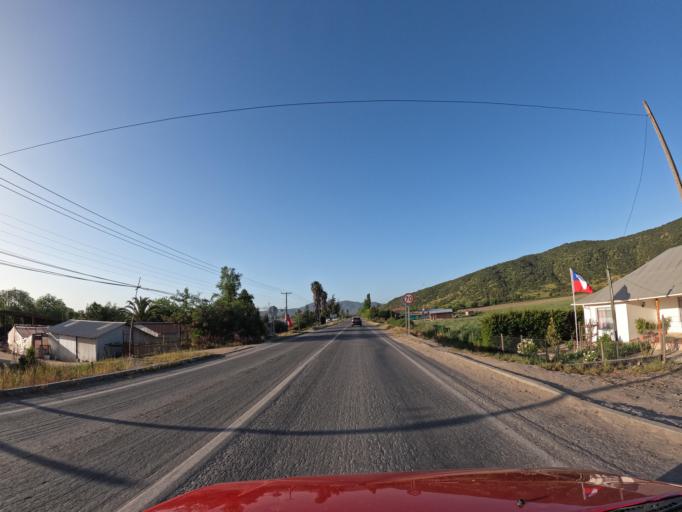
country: CL
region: O'Higgins
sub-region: Provincia de Colchagua
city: Santa Cruz
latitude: -34.4138
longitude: -71.3728
